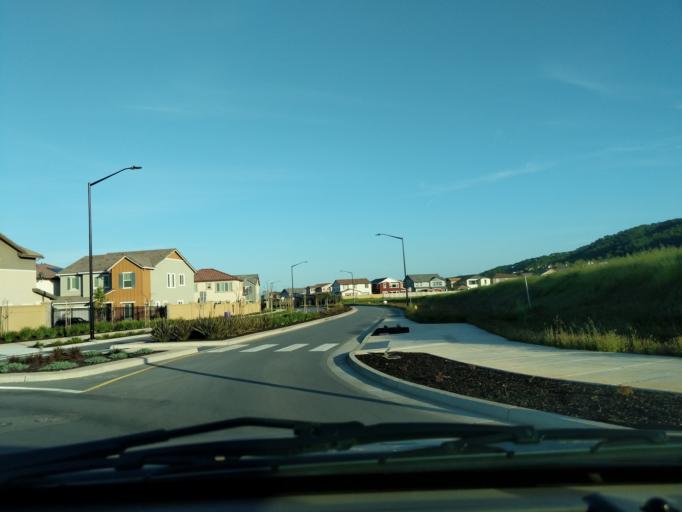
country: US
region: California
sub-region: Santa Clara County
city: Gilroy
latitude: 36.9906
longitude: -121.5854
